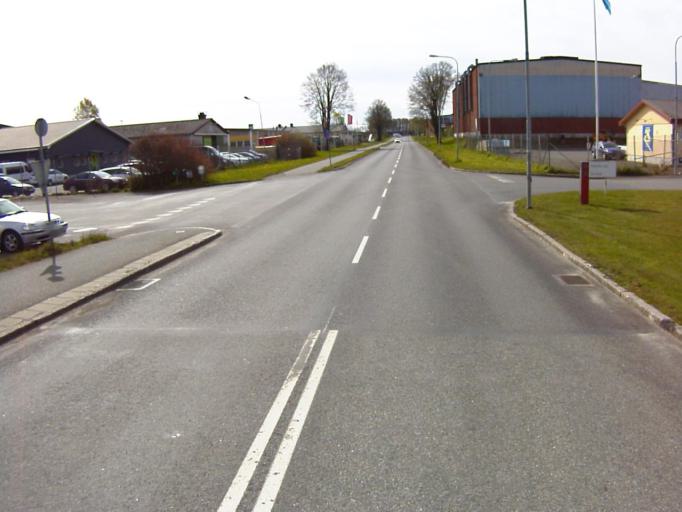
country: SE
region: Skane
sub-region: Kristianstads Kommun
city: Kristianstad
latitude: 56.0164
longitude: 14.1531
